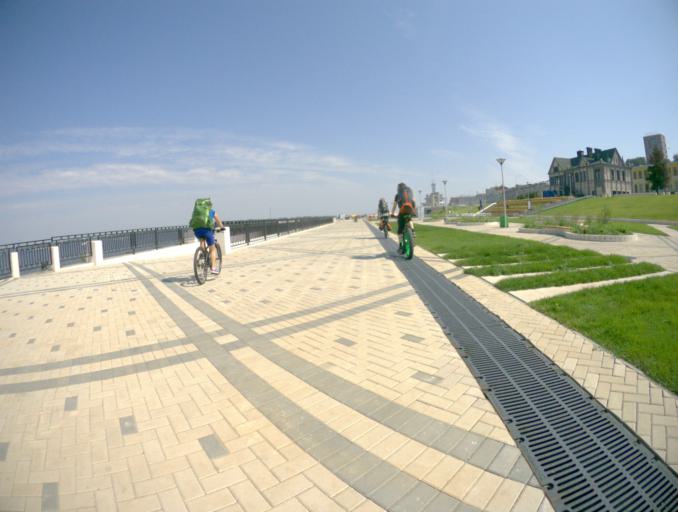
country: RU
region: Nizjnij Novgorod
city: Nizhniy Novgorod
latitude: 56.3283
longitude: 43.9826
